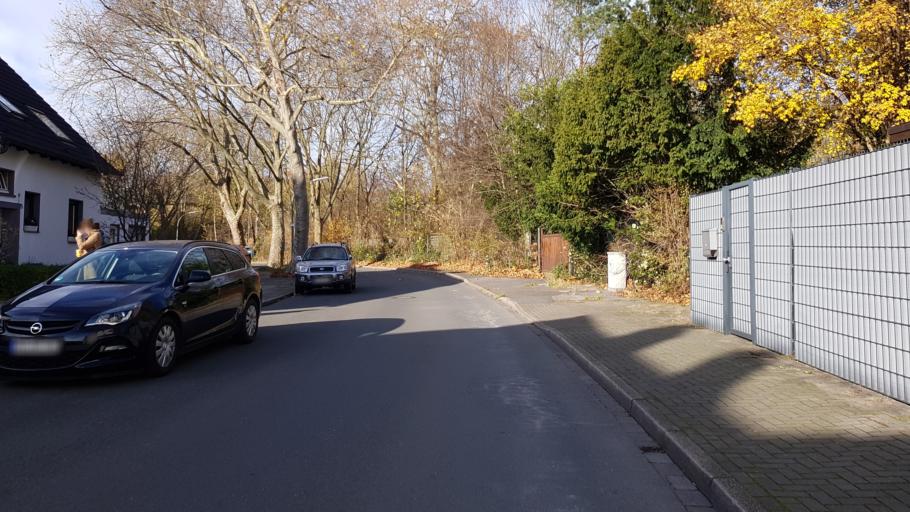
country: DE
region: North Rhine-Westphalia
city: Bochum-Hordel
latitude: 51.4914
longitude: 7.1485
